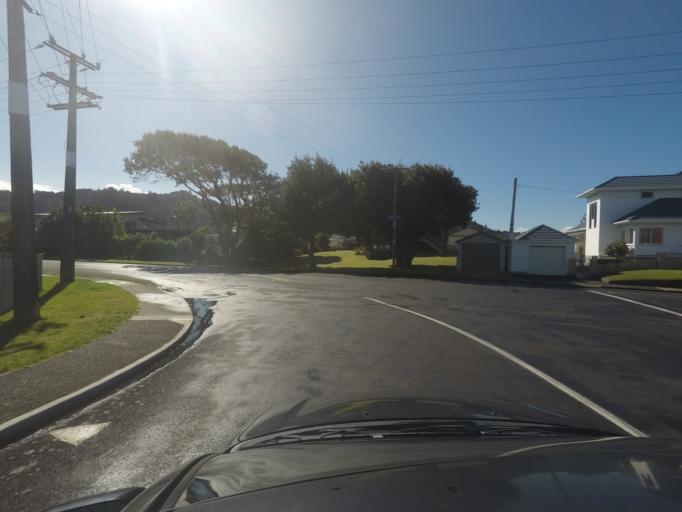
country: NZ
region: Bay of Plenty
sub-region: Western Bay of Plenty District
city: Waihi Beach
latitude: -37.4028
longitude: 175.9401
